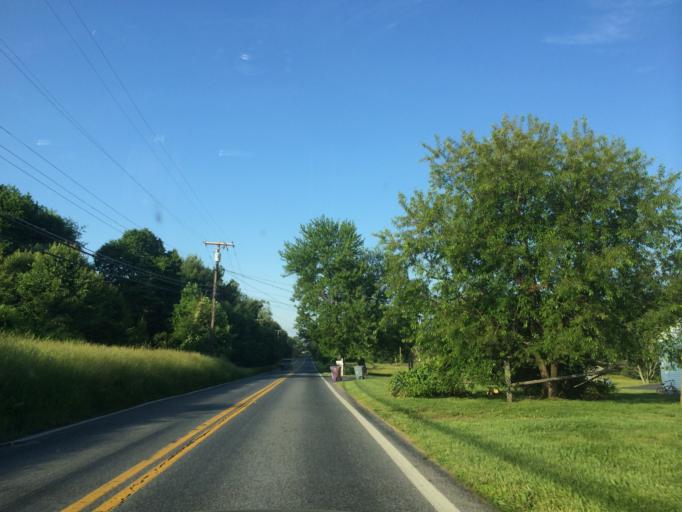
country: US
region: Maryland
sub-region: Howard County
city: Highland
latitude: 39.1818
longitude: -76.9321
